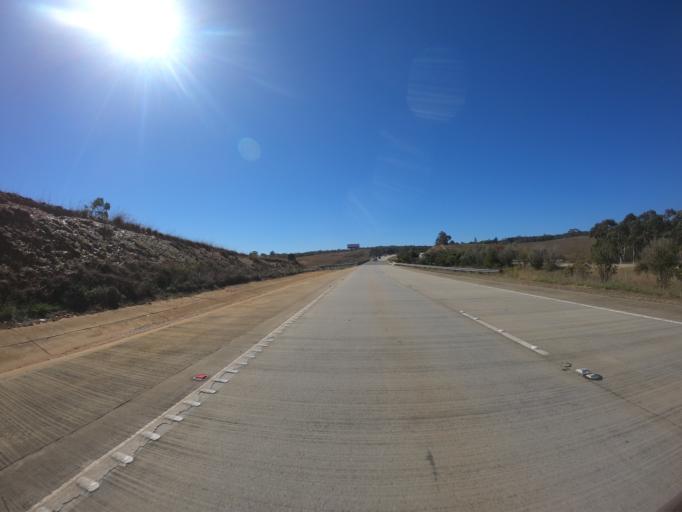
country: AU
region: New South Wales
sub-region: Yass Valley
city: Gundaroo
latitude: -35.1201
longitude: 149.3470
